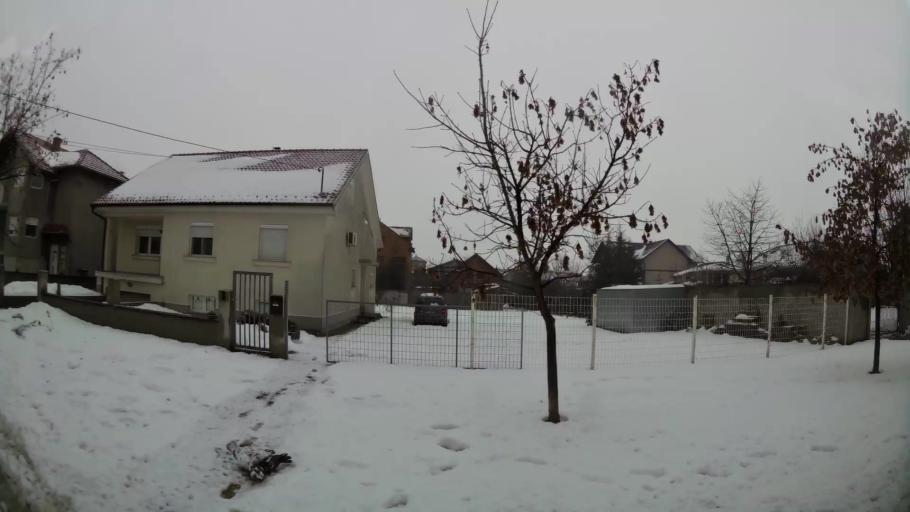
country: RS
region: Central Serbia
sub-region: Belgrade
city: Zemun
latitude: 44.8478
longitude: 20.3441
